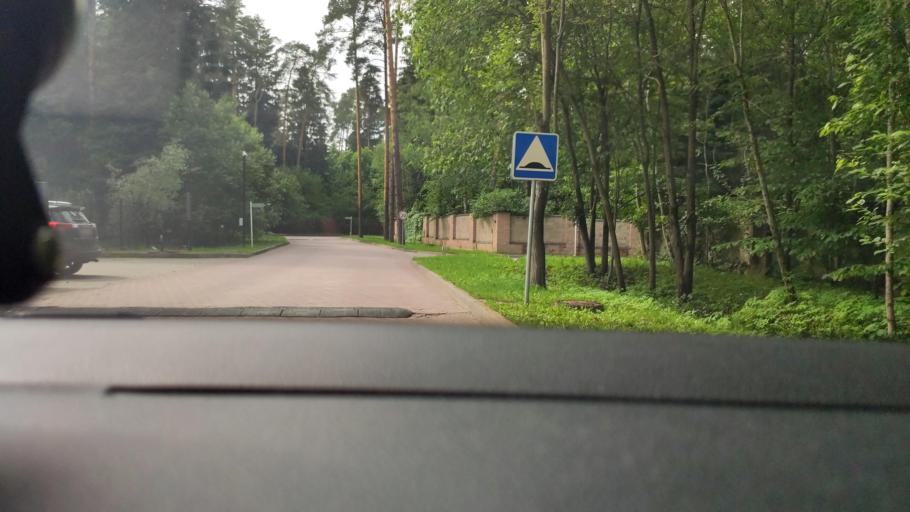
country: RU
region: Moskovskaya
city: Nikolina Gora
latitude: 55.7362
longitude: 37.0721
